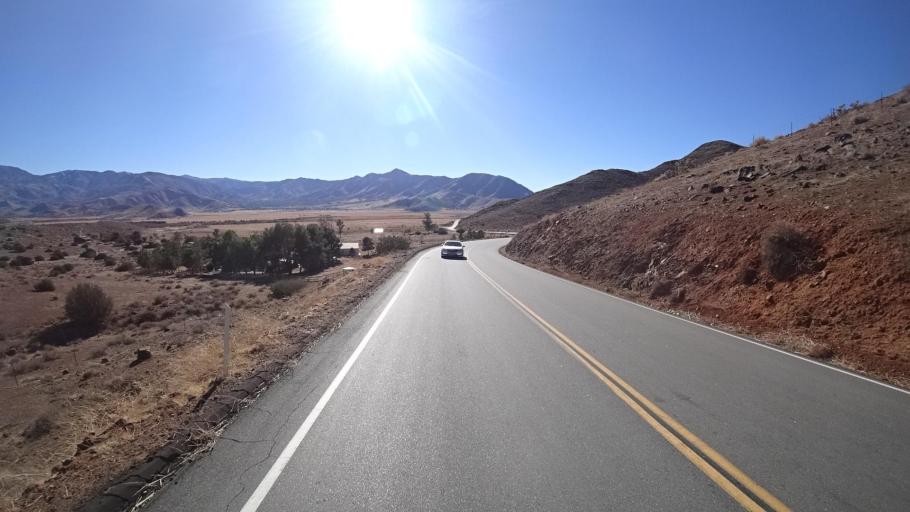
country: US
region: California
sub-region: Kern County
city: Wofford Heights
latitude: 35.6813
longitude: -118.3928
